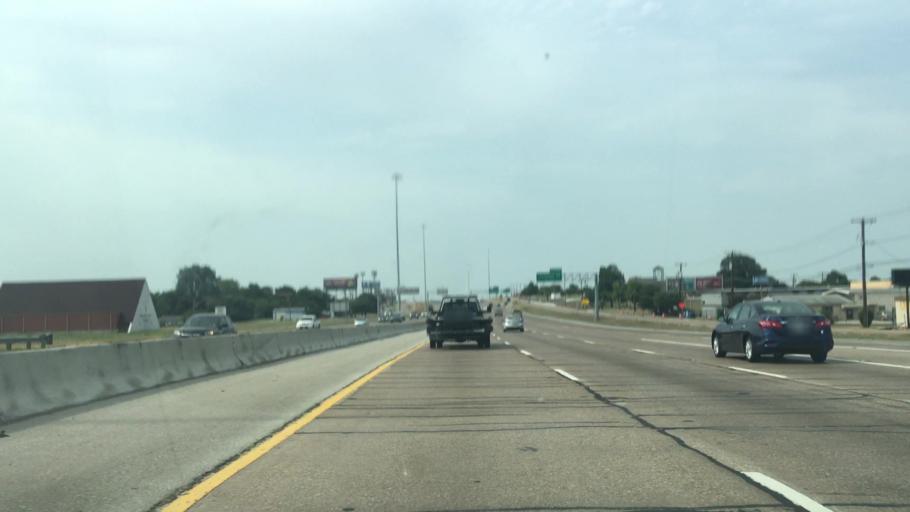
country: US
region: Texas
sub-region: Dallas County
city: DeSoto
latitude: 32.6663
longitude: -96.8229
